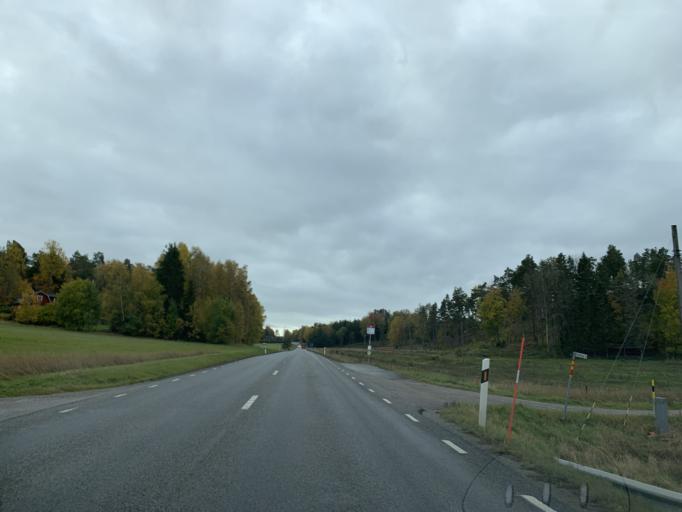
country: SE
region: Stockholm
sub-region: Nynashamns Kommun
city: Osmo
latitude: 59.0022
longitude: 17.8014
